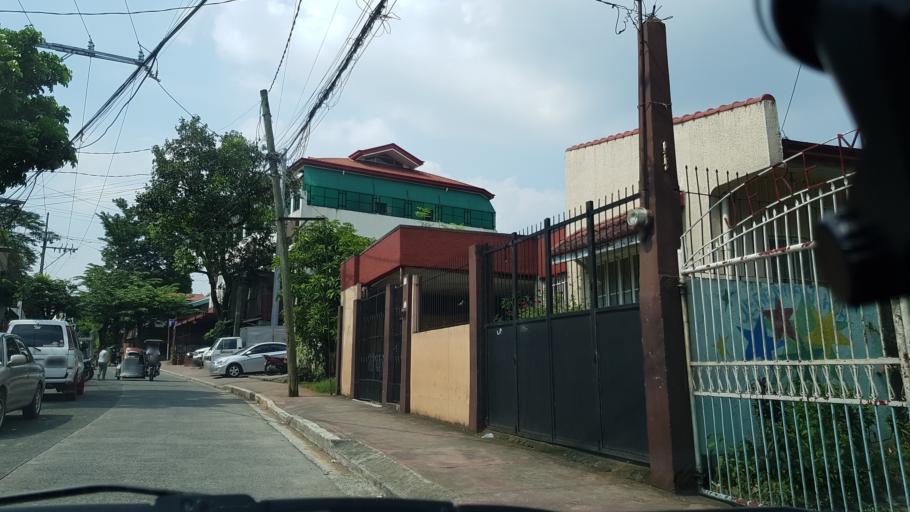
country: PH
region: Calabarzon
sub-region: Province of Rizal
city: Antipolo
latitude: 14.6534
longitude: 121.1200
